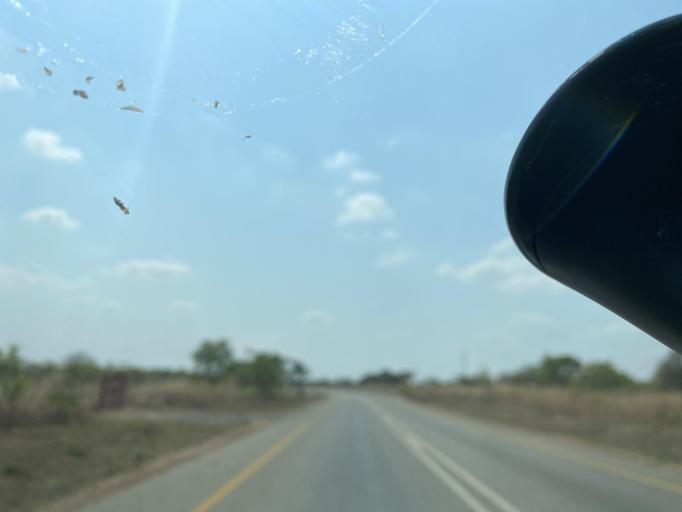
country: ZM
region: Lusaka
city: Chongwe
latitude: -15.5365
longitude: 28.6511
